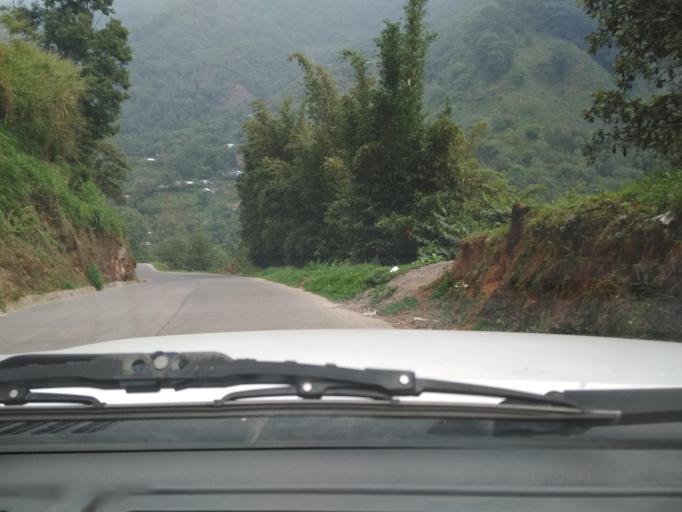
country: MX
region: Veracruz
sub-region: La Perla
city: Barrio de San Miguel
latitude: 18.9333
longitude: -97.1263
